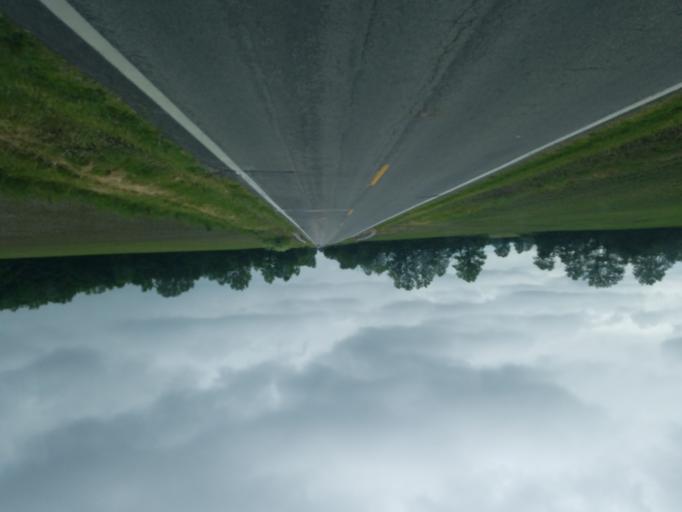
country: US
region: Ohio
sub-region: Morrow County
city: Cardington
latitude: 40.5305
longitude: -82.9788
